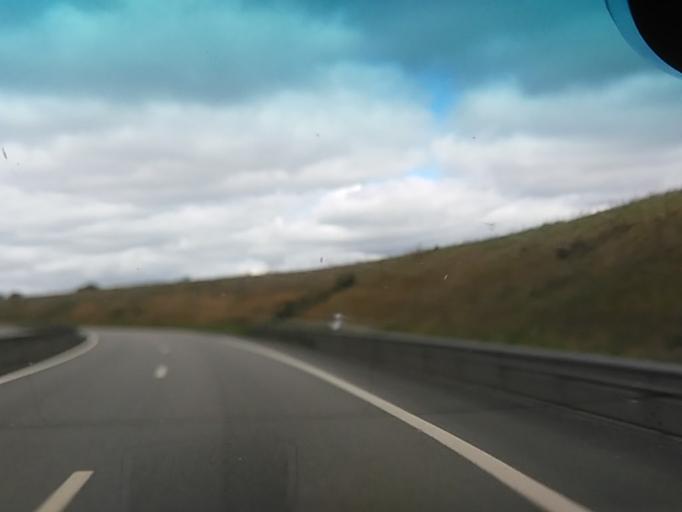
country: FR
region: Haute-Normandie
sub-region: Departement de l'Eure
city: Bourg-Achard
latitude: 49.3585
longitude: 0.8349
